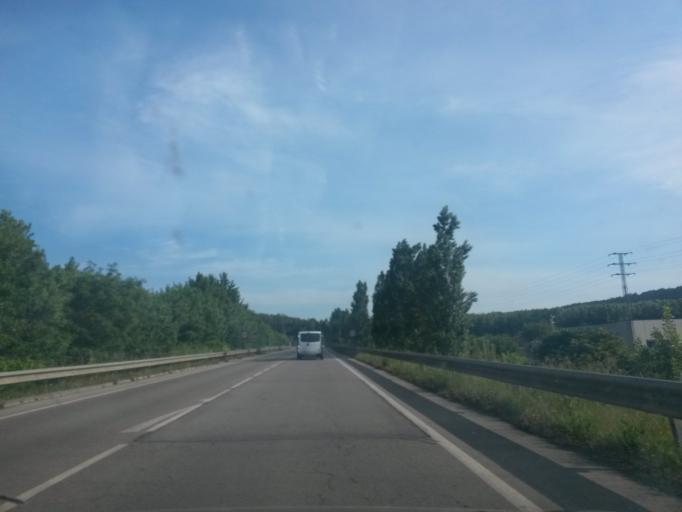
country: ES
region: Catalonia
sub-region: Provincia de Girona
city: la Cellera de Ter
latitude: 41.9728
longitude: 2.6240
